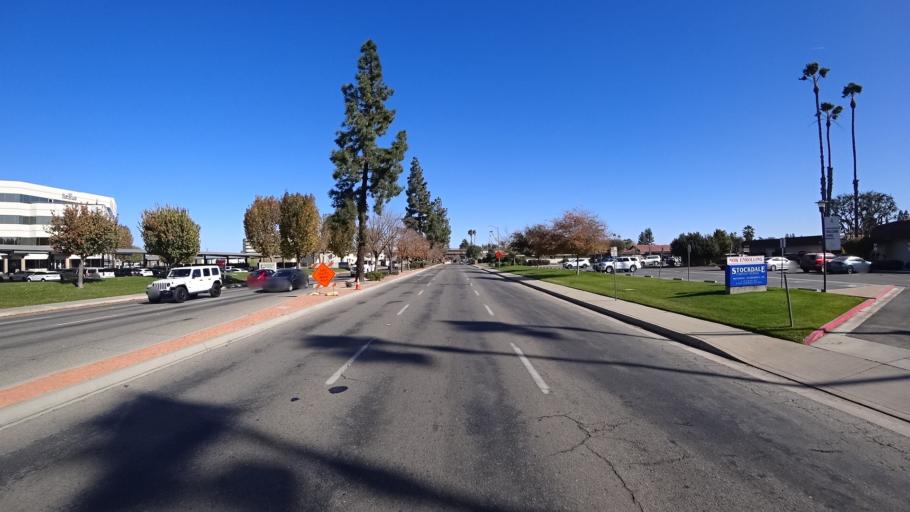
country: US
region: California
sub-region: Kern County
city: Bakersfield
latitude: 35.3643
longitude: -119.0563
